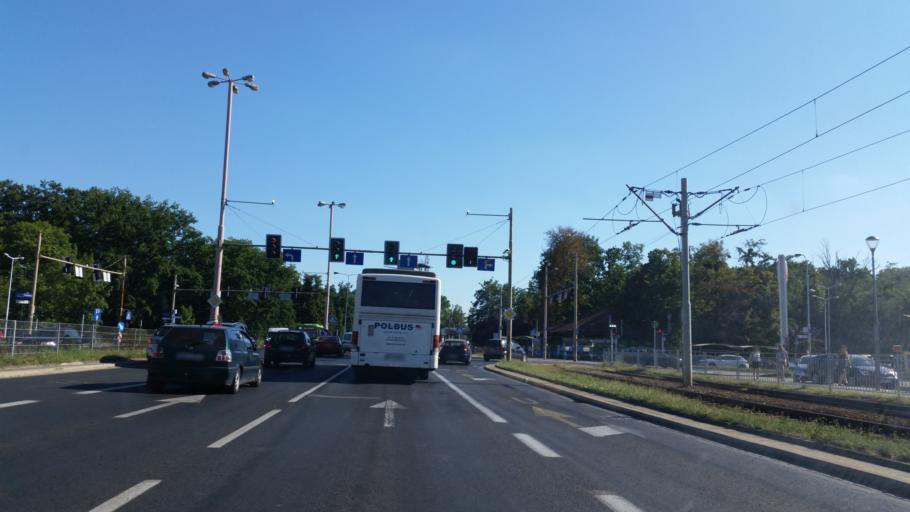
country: PL
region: Lower Silesian Voivodeship
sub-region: Powiat wroclawski
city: Wroclaw
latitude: 51.0758
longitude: 17.0073
